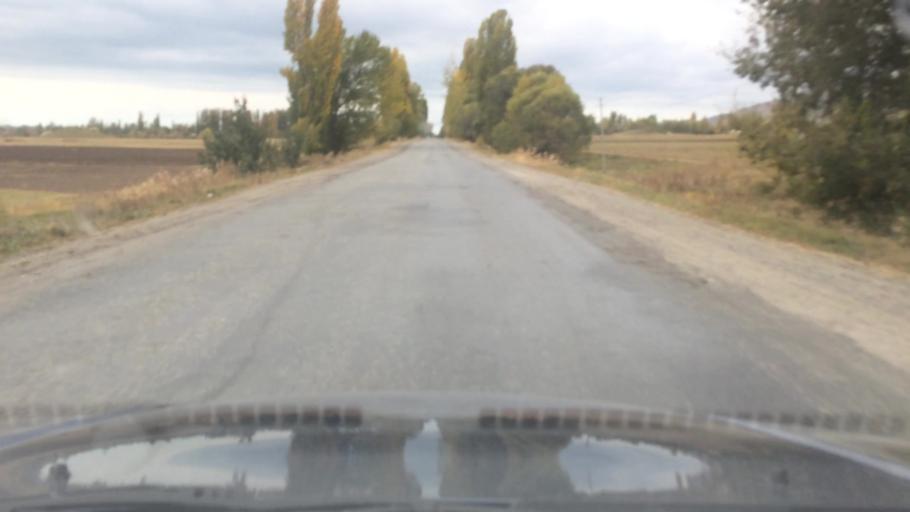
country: KG
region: Ysyk-Koel
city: Tyup
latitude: 42.7733
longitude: 78.1975
